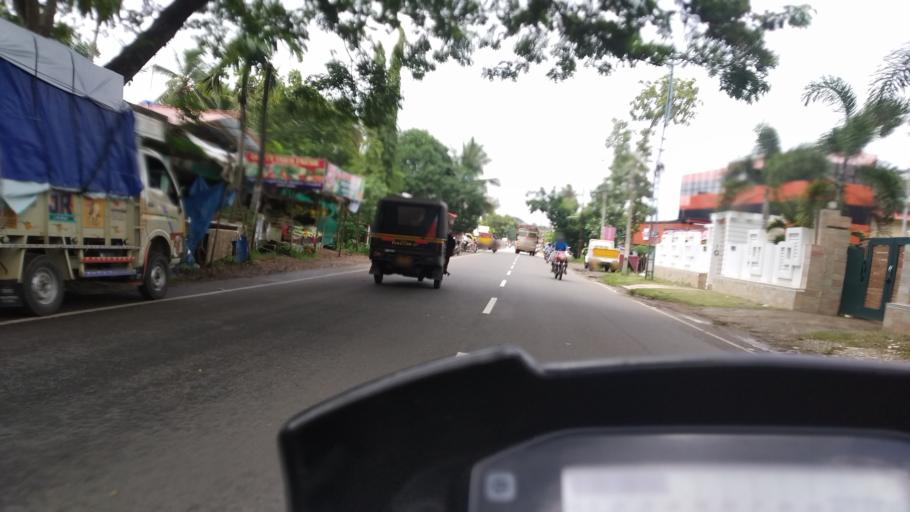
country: IN
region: Kerala
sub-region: Ernakulam
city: Aluva
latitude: 10.1289
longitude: 76.3030
